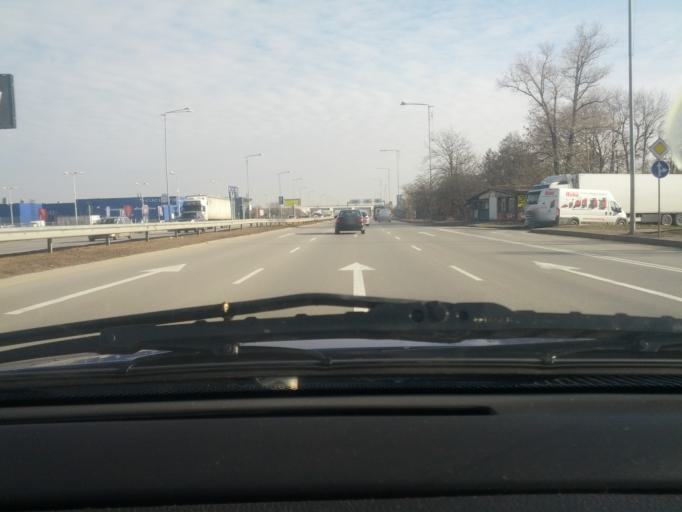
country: BG
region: Sofia-Capital
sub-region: Stolichna Obshtina
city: Sofia
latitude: 42.7088
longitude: 23.4320
